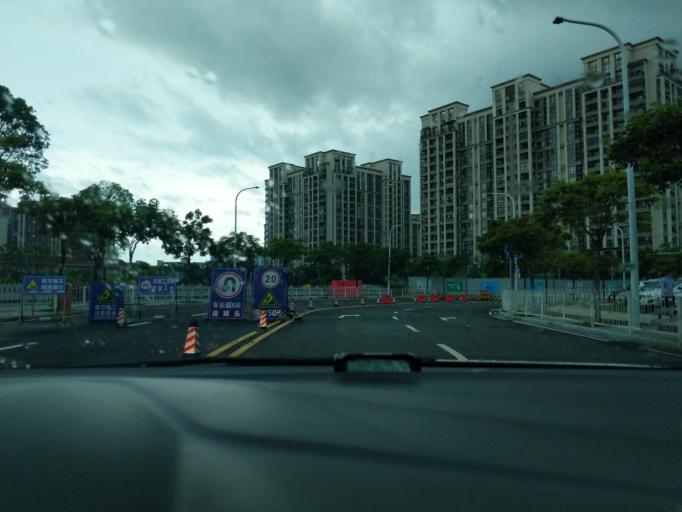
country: CN
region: Guangdong
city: Huangge
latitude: 22.7972
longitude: 113.5162
